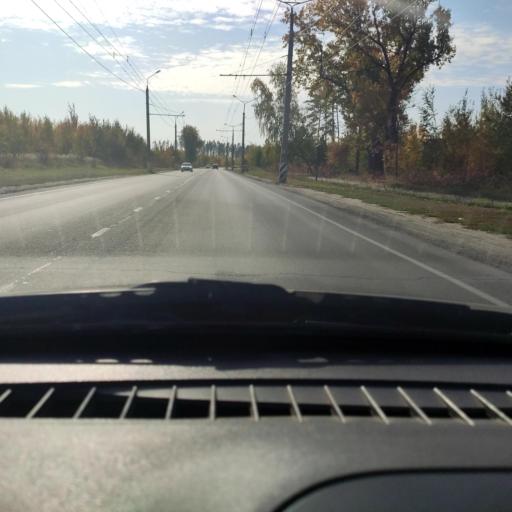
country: RU
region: Samara
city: Tol'yatti
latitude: 53.4852
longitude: 49.3807
